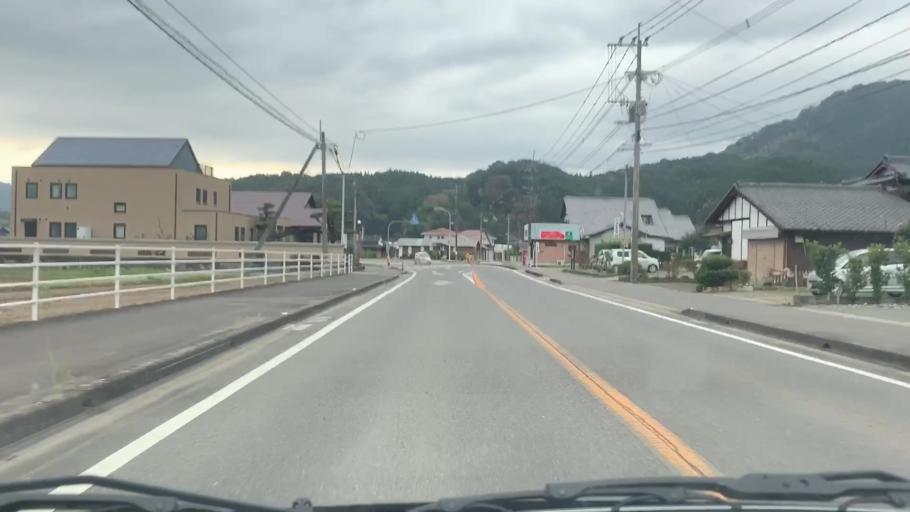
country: JP
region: Saga Prefecture
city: Takeocho-takeo
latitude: 33.1698
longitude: 130.0502
